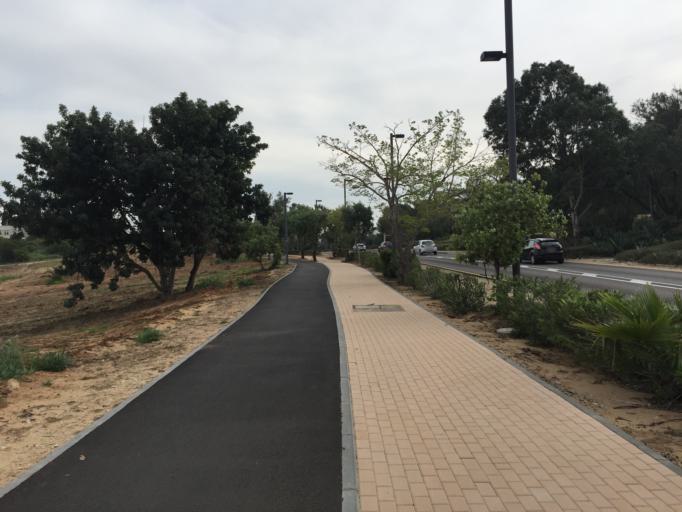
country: IL
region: Haifa
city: Qesarya
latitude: 32.5077
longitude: 34.9038
